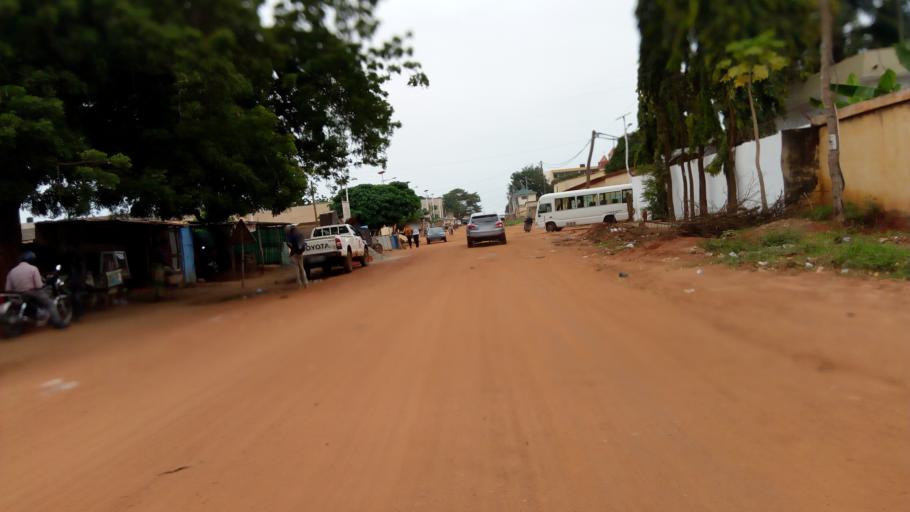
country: TG
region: Maritime
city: Lome
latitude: 6.1608
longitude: 1.2214
